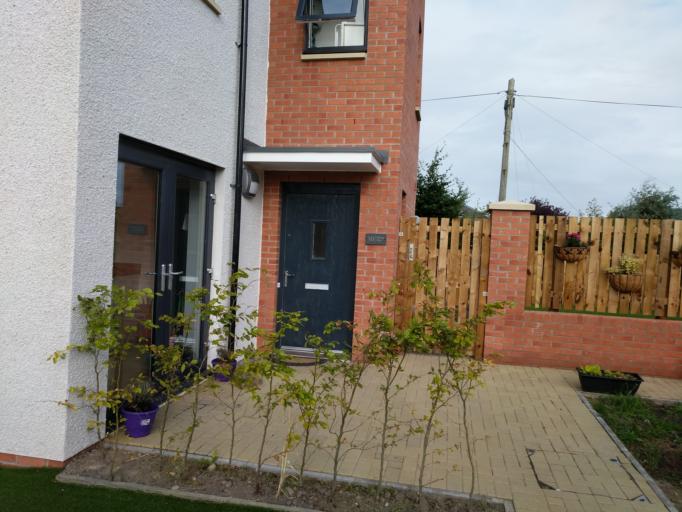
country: GB
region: Scotland
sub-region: Edinburgh
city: Colinton
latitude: 55.9313
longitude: -3.2443
